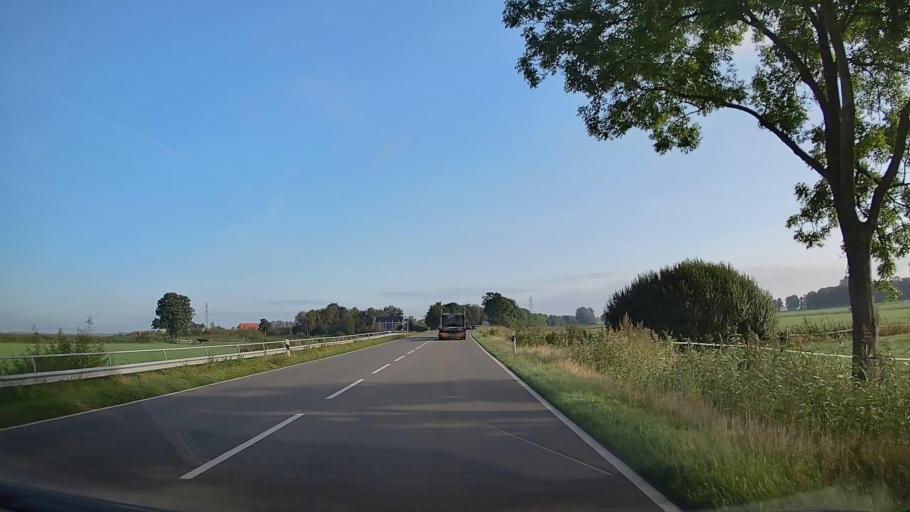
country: DE
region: Lower Saxony
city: Rastede
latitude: 53.2554
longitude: 8.3033
